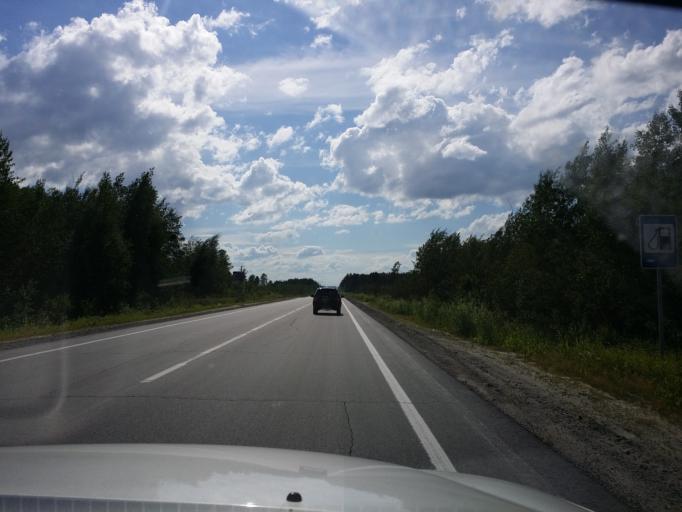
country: RU
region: Khanty-Mansiyskiy Avtonomnyy Okrug
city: Nizhnevartovsk
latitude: 60.9551
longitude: 76.7113
